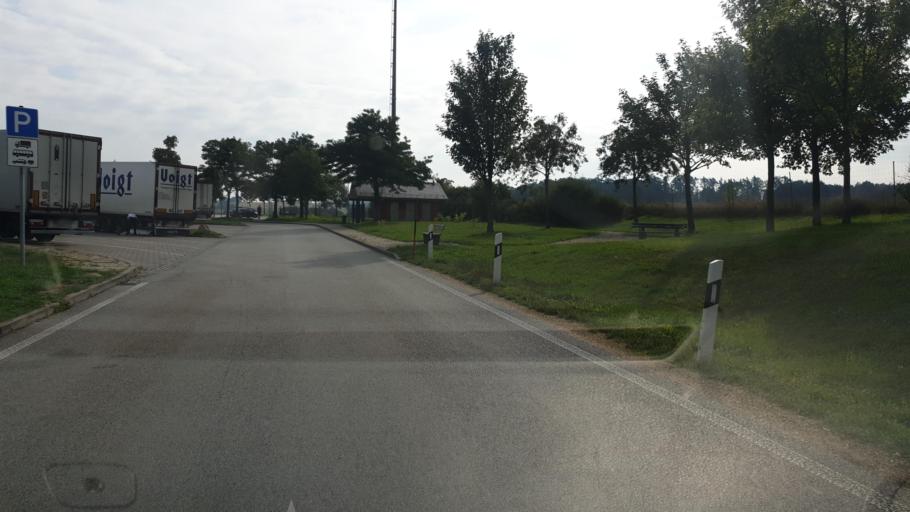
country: DE
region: Saxony
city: Kodersdorf
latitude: 51.2190
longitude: 14.8706
